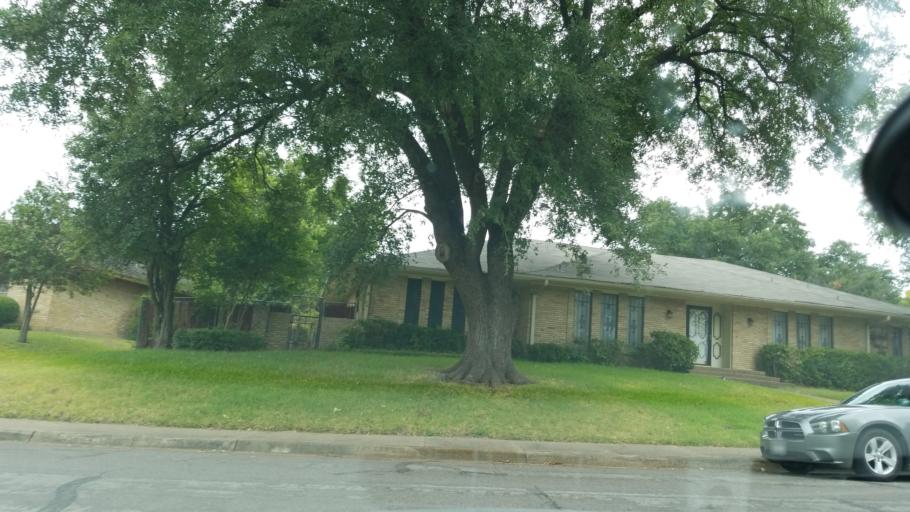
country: US
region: Texas
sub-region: Dallas County
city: Duncanville
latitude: 32.6654
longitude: -96.8536
